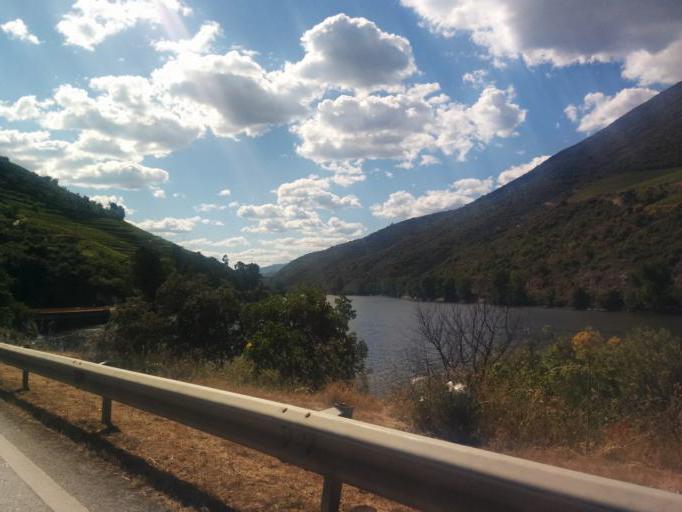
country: PT
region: Viseu
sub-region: Armamar
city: Armamar
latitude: 41.1407
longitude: -7.6975
